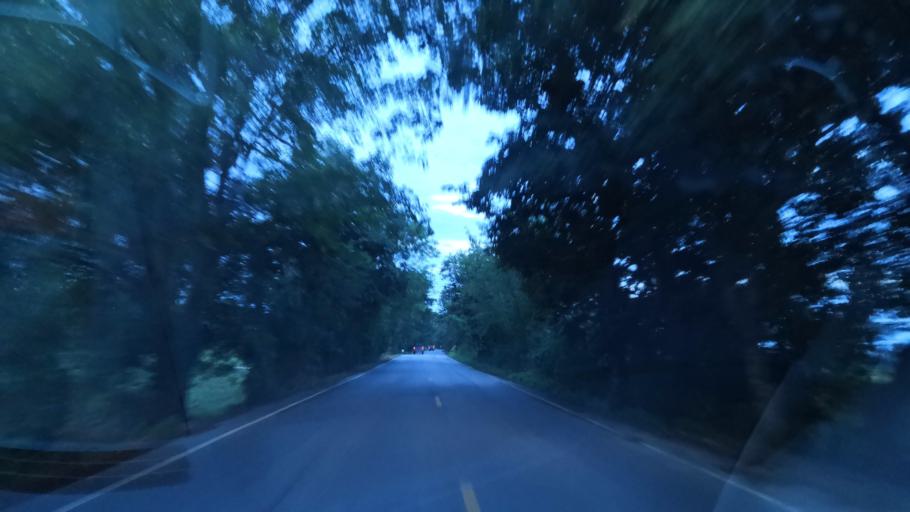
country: TH
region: Chiang Rai
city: Wiang Chai
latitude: 19.9503
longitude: 99.9333
